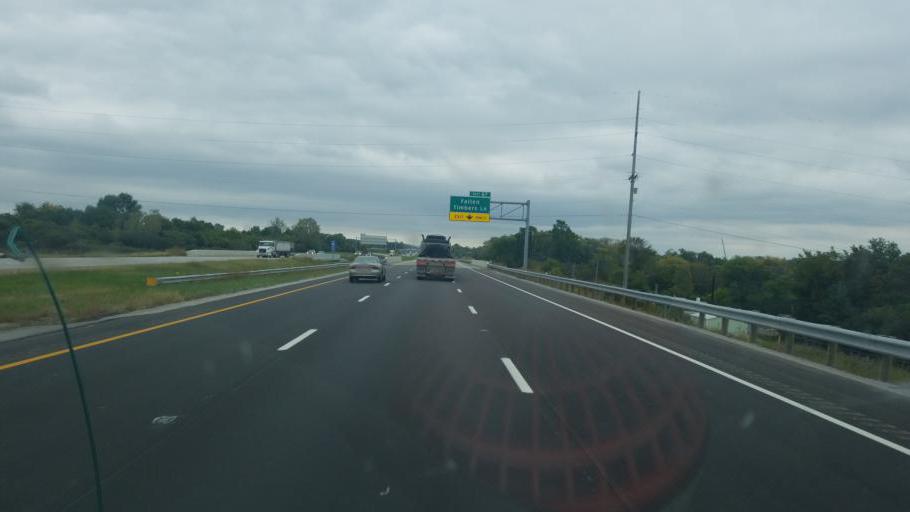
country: US
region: Ohio
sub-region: Lucas County
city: Waterville
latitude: 41.5348
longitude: -83.7111
